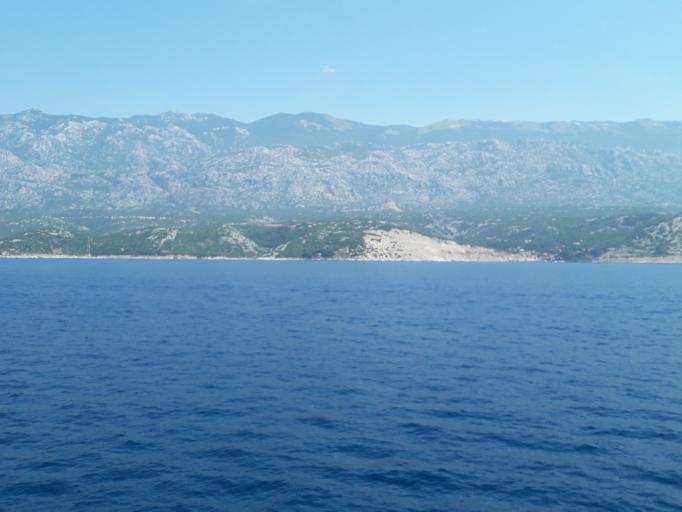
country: HR
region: Primorsko-Goranska
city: Banjol
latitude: 44.7044
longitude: 14.8719
